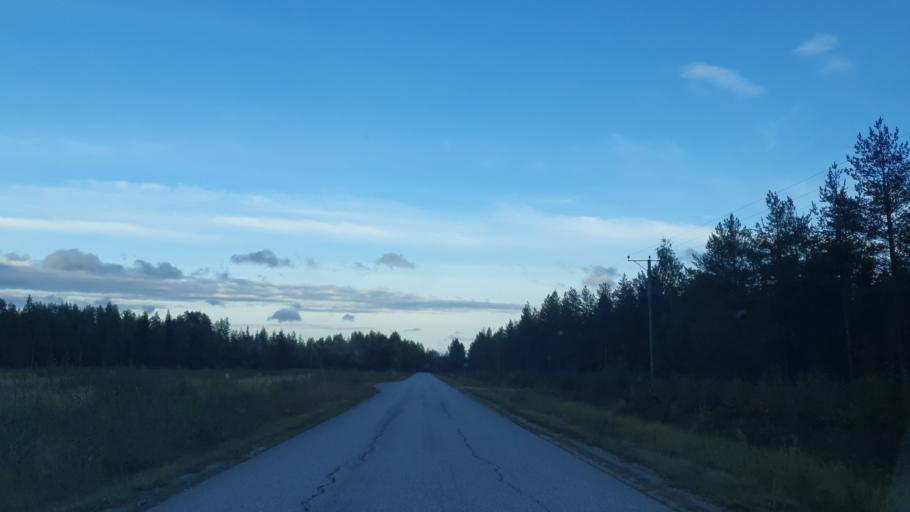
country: FI
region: Kainuu
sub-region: Kehys-Kainuu
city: Kuhmo
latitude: 64.4182
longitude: 29.9157
